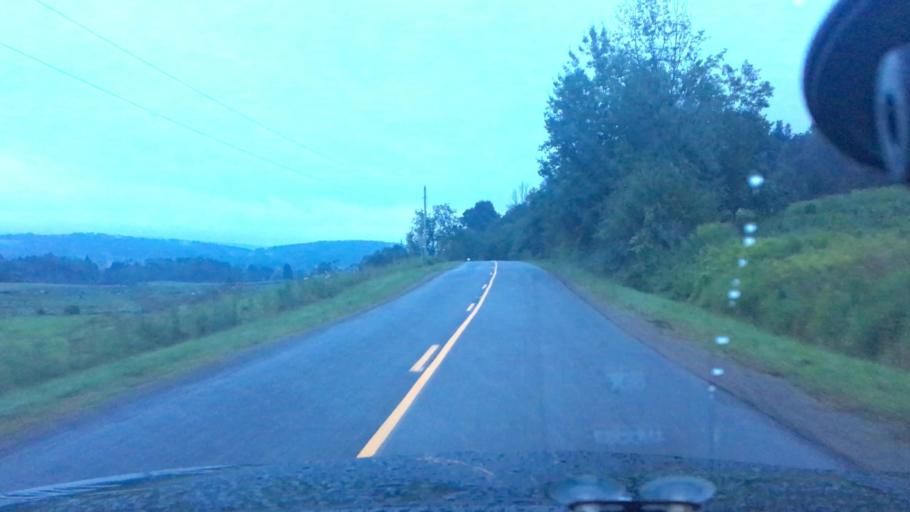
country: US
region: New York
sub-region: Cattaraugus County
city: Cattaraugus
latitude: 42.2474
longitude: -78.8909
